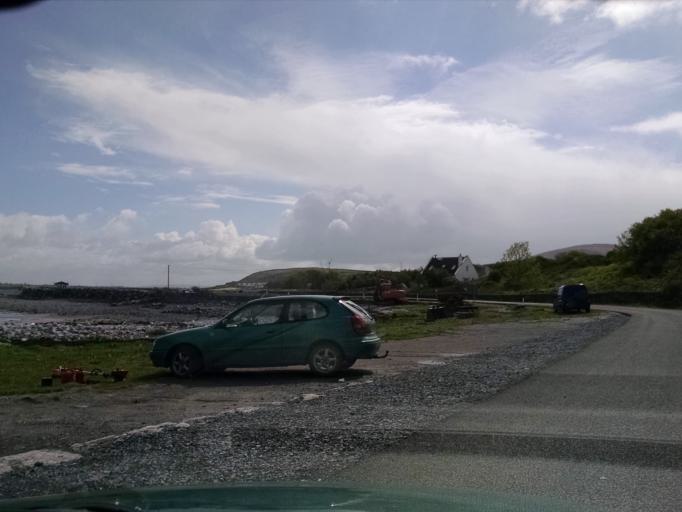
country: IE
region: Connaught
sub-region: County Galway
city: Bearna
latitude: 53.1571
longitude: -9.0885
